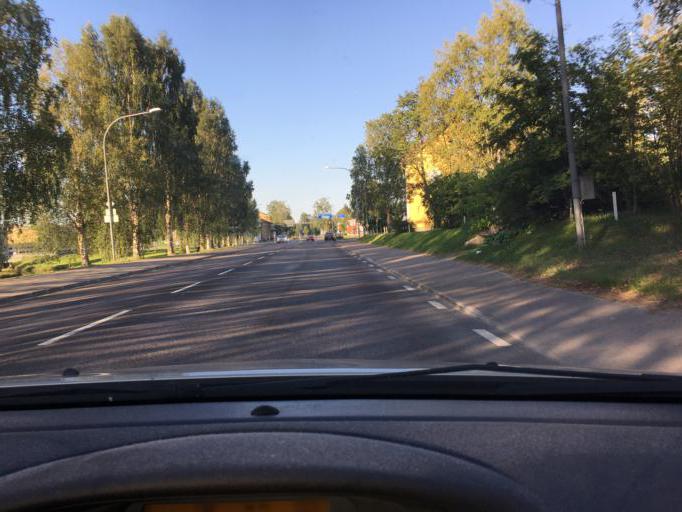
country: SE
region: Norrbotten
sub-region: Bodens Kommun
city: Boden
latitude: 65.8236
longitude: 21.6938
